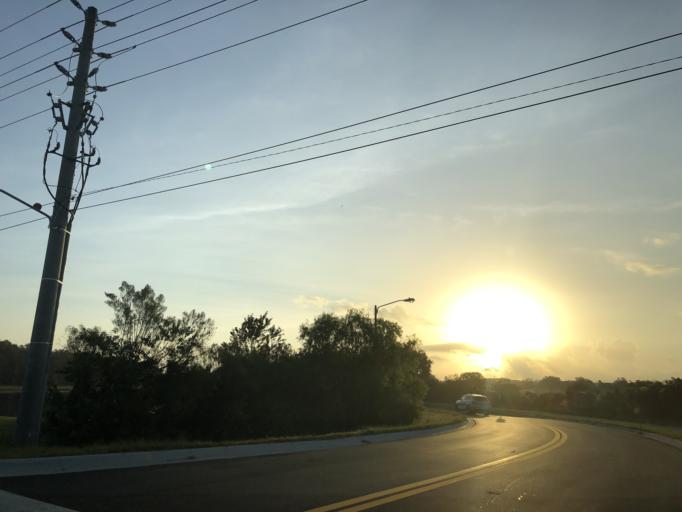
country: US
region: Florida
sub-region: Osceola County
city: Kissimmee
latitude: 28.3194
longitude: -81.4426
